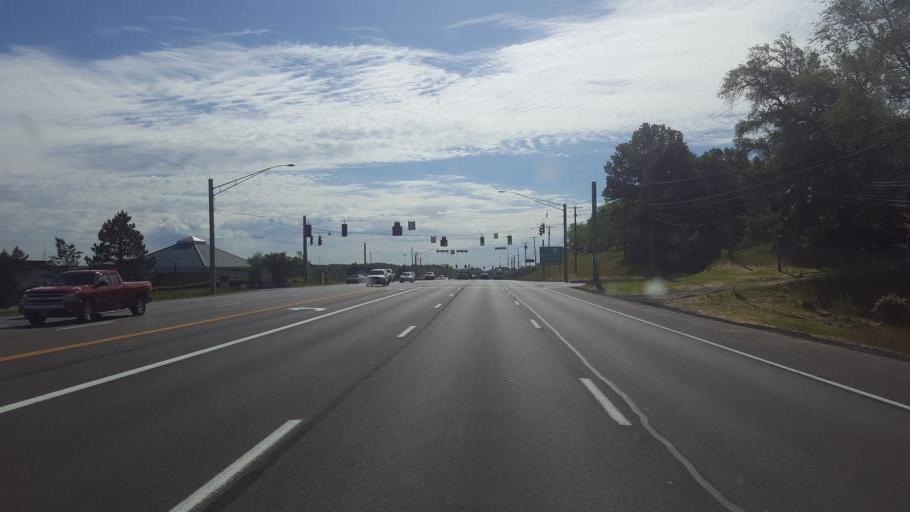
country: US
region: Ohio
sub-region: Summit County
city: Montrose-Ghent
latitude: 41.1359
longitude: -81.6608
